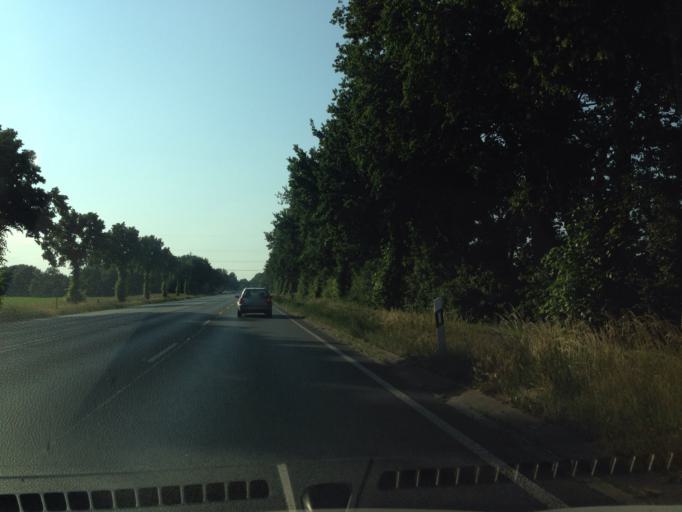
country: DE
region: North Rhine-Westphalia
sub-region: Regierungsbezirk Munster
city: Muenster
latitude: 51.9818
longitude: 7.5926
